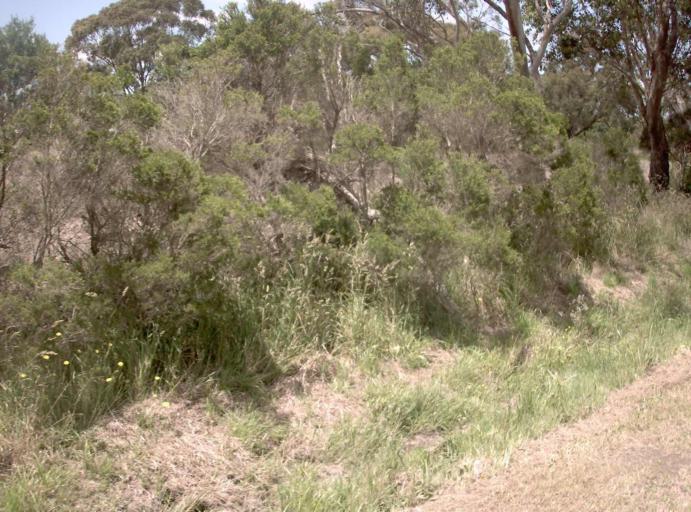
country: AU
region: Victoria
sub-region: Bass Coast
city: North Wonthaggi
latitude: -38.6570
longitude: 146.0191
